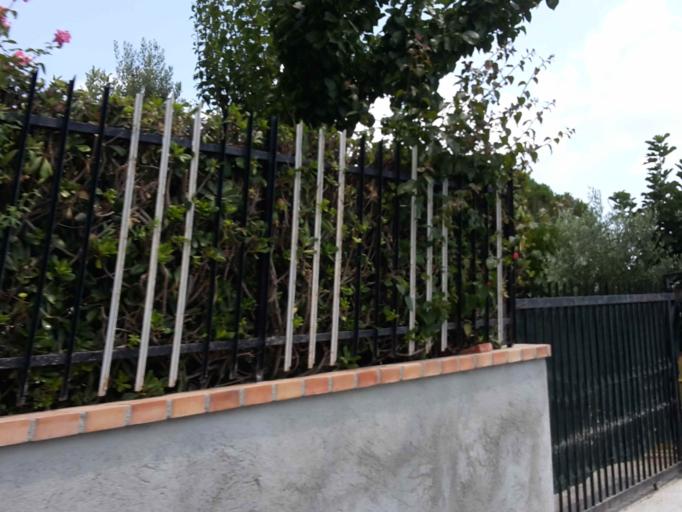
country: IT
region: Calabria
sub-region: Provincia di Reggio Calabria
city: Condofuri
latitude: 37.9871
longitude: 15.8407
